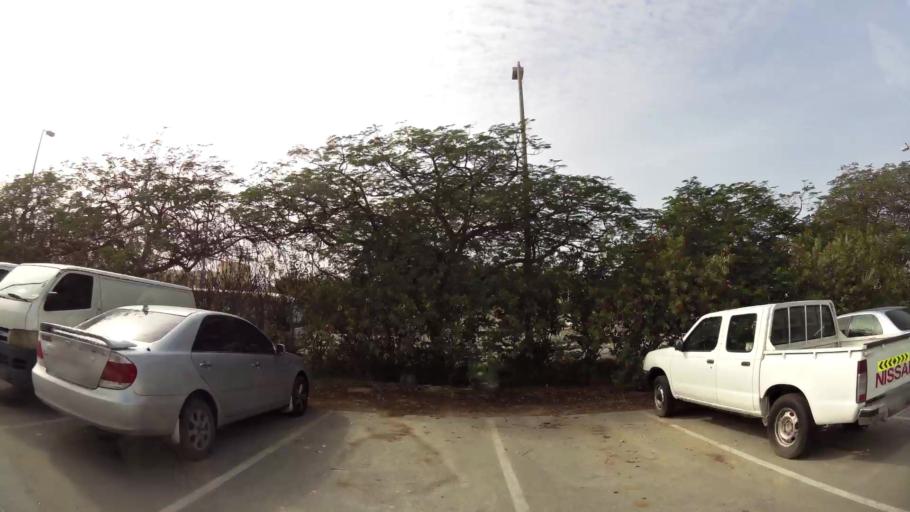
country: AE
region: Abu Dhabi
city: Abu Dhabi
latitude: 24.5977
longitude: 54.7030
